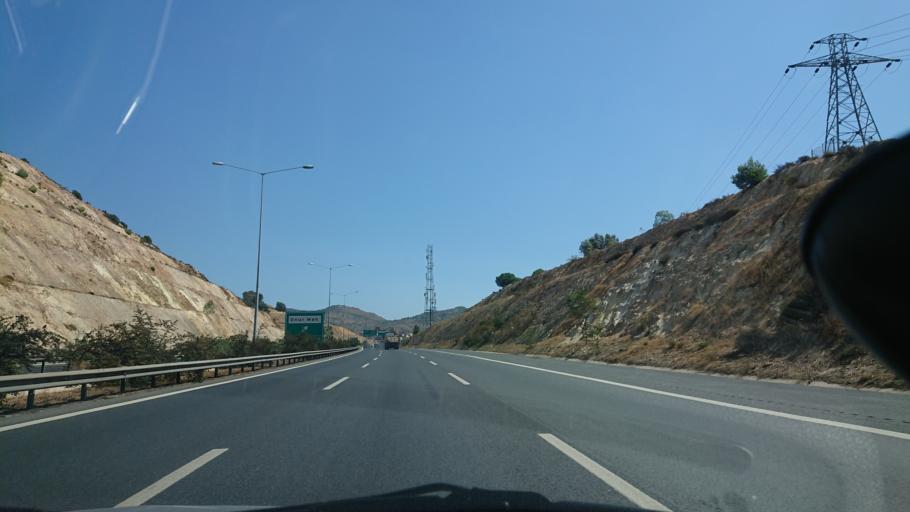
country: TR
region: Izmir
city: Karsiyaka
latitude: 38.4860
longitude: 27.1223
